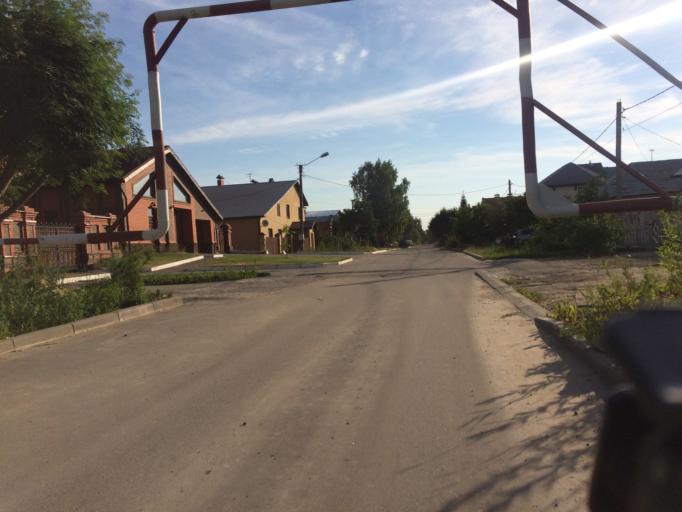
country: RU
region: Mariy-El
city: Yoshkar-Ola
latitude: 56.6466
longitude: 47.9117
